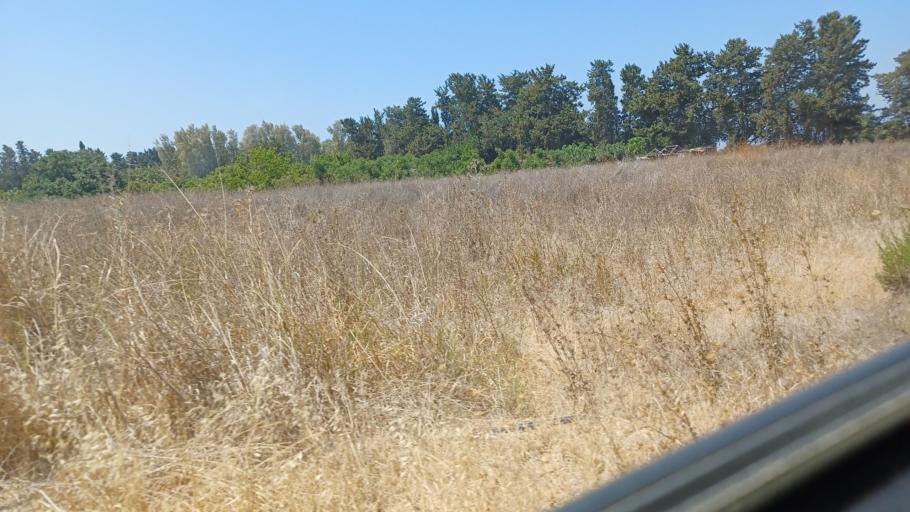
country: CY
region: Pafos
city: Paphos
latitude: 34.7334
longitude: 32.4807
